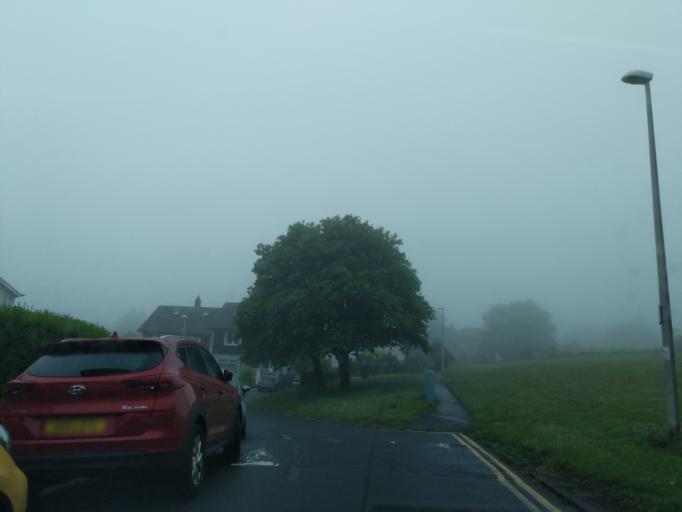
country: GB
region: Scotland
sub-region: West Lothian
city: Seafield
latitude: 55.9441
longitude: -3.1451
